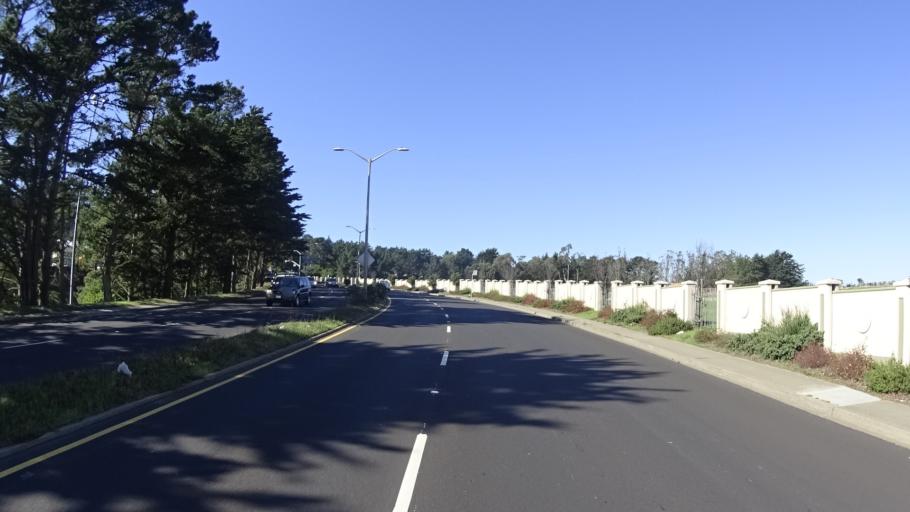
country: US
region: California
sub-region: San Mateo County
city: Colma
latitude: 37.6655
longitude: -122.4725
